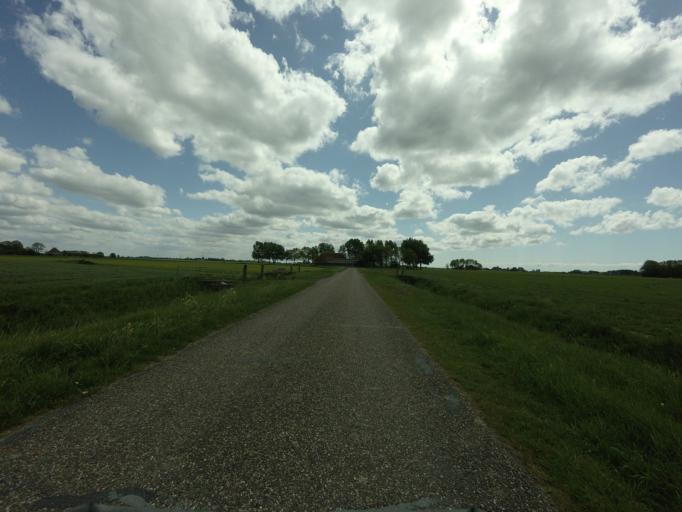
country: NL
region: Friesland
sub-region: Gemeente Franekeradeel
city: Tzum
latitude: 53.1384
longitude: 5.5578
